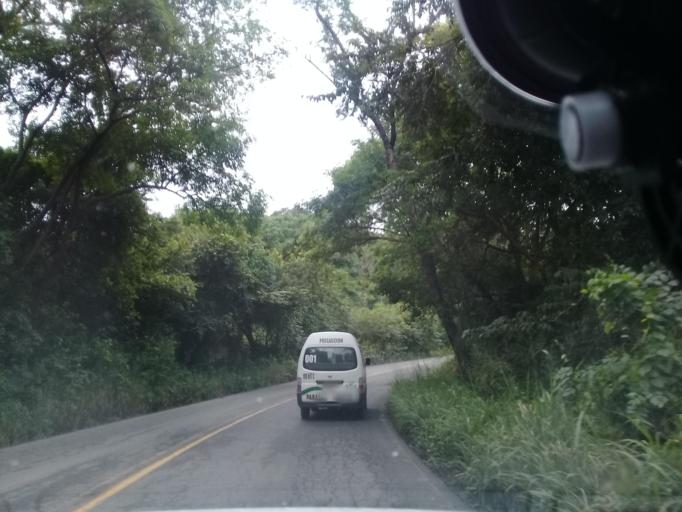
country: MX
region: Hidalgo
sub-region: Huejutla de Reyes
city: Parque de Poblamiento Solidaridad
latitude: 21.1969
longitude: -98.3898
